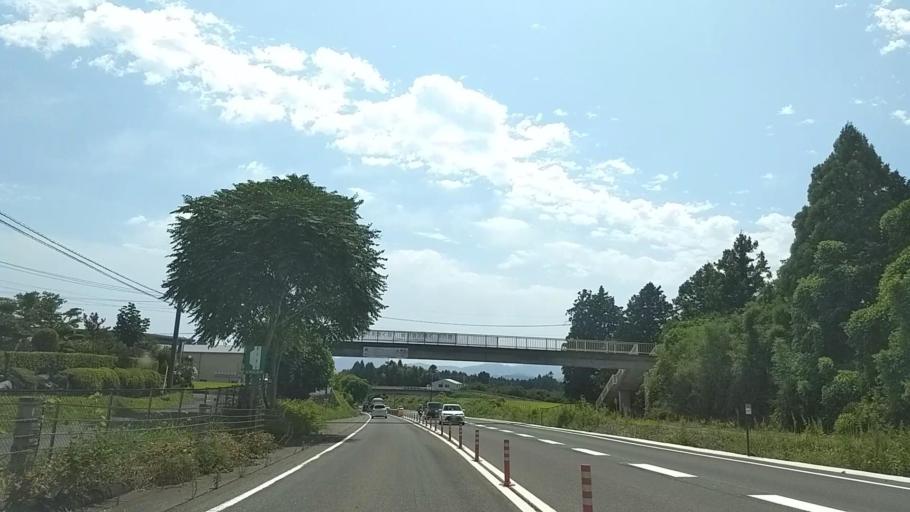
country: JP
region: Shizuoka
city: Fujinomiya
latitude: 35.2793
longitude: 138.6123
